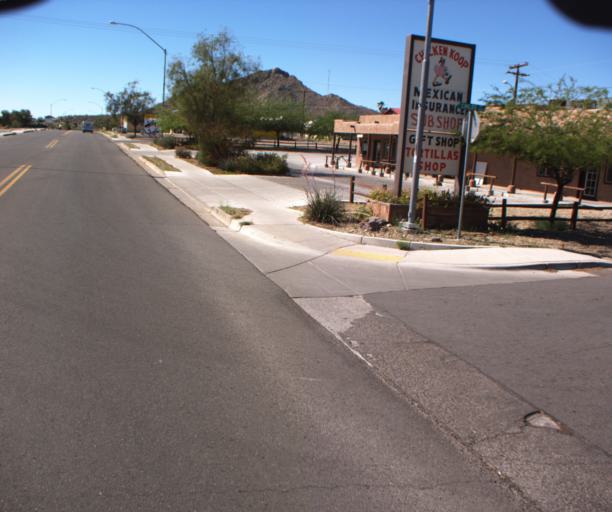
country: US
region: Arizona
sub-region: Pima County
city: Ajo
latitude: 32.3813
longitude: -112.8724
